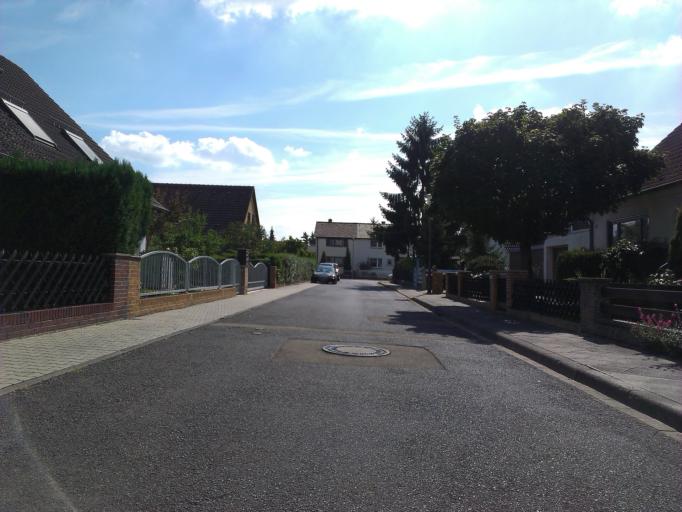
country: DE
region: Baden-Wuerttemberg
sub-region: Karlsruhe Region
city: Mannheim
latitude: 49.5397
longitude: 8.4799
